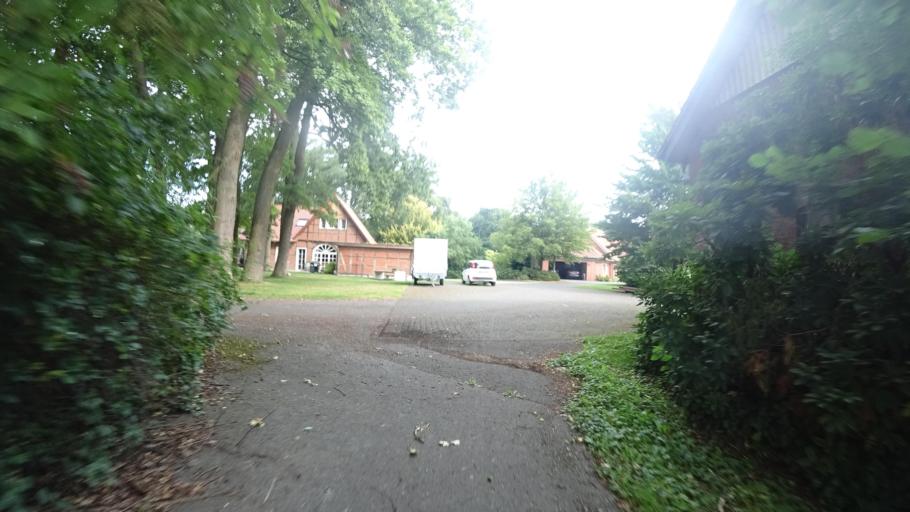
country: DE
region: North Rhine-Westphalia
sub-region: Regierungsbezirk Detmold
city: Guetersloh
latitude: 51.9352
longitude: 8.4150
